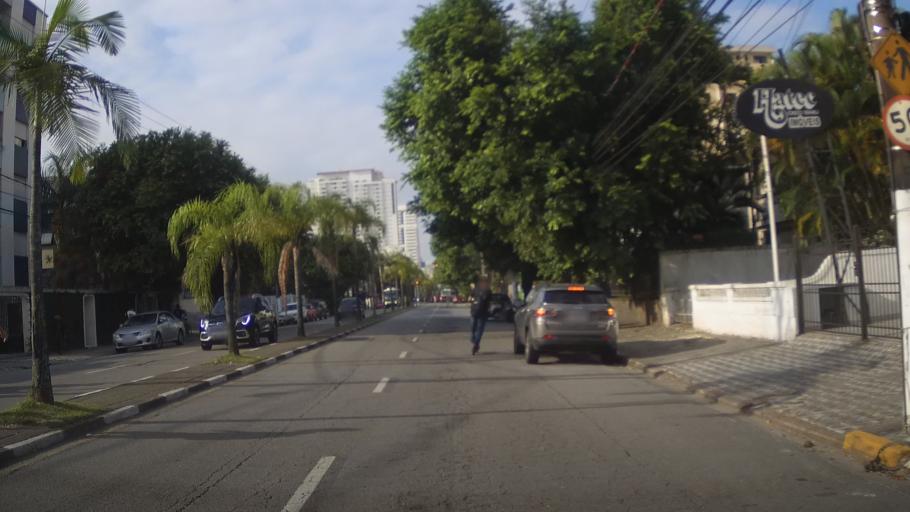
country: BR
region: Sao Paulo
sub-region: Santos
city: Santos
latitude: -23.9583
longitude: -46.3230
